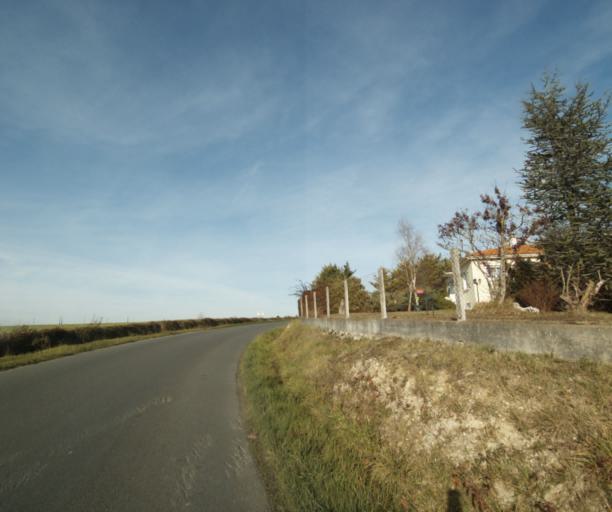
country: FR
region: Poitou-Charentes
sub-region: Departement de la Charente-Maritime
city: Chaniers
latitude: 45.7237
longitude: -0.5574
